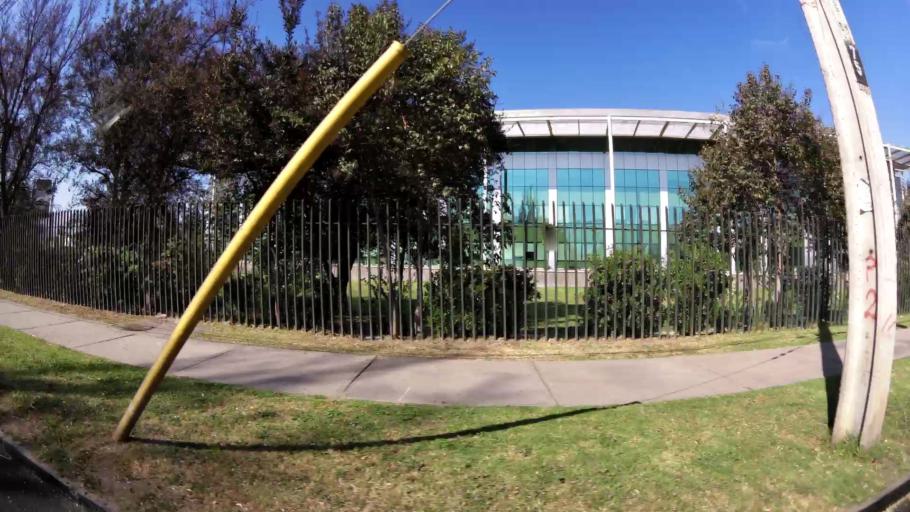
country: CL
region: Santiago Metropolitan
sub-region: Provincia de Chacabuco
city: Chicureo Abajo
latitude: -33.3611
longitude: -70.6712
